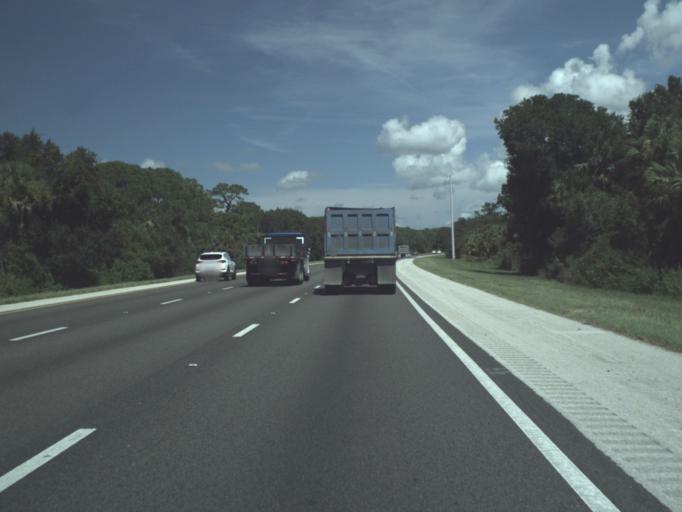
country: US
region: Florida
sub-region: Sarasota County
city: Vamo
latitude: 27.2247
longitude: -82.4499
